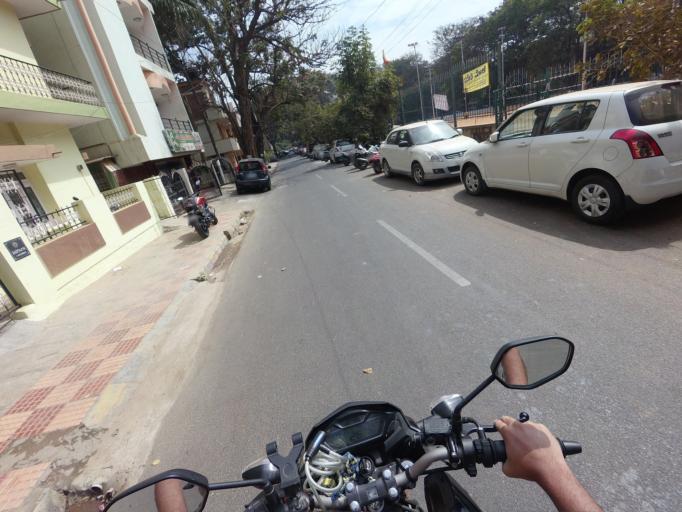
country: IN
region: Karnataka
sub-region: Bangalore Urban
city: Bangalore
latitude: 12.9716
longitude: 77.5428
